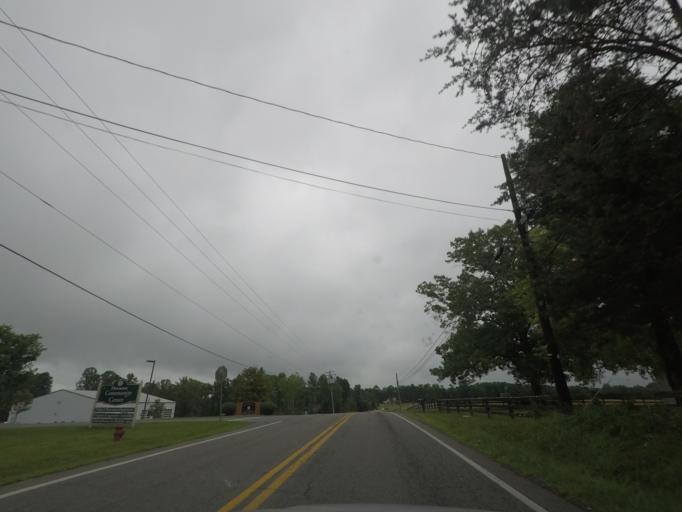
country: US
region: Virginia
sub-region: Fluvanna County
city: Weber City
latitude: 37.7737
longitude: -78.2519
